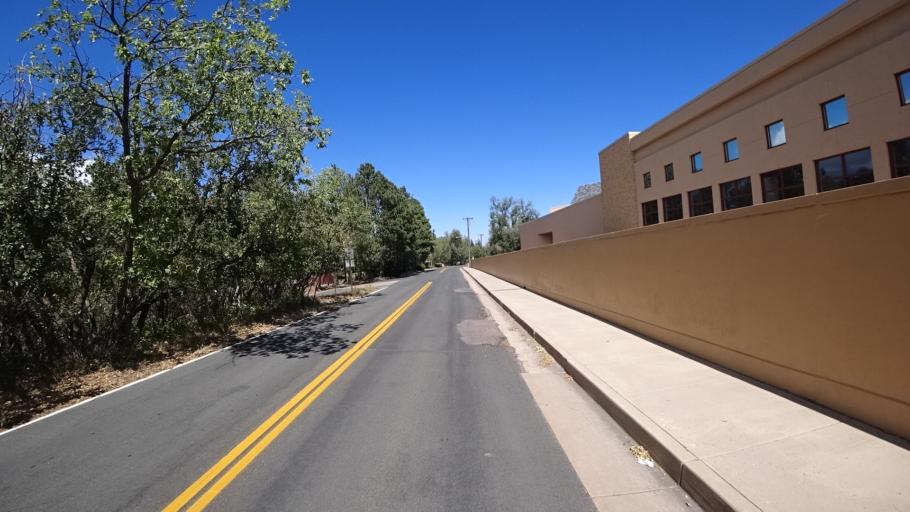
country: US
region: Colorado
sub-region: El Paso County
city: Colorado Springs
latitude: 38.7909
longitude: -104.8558
